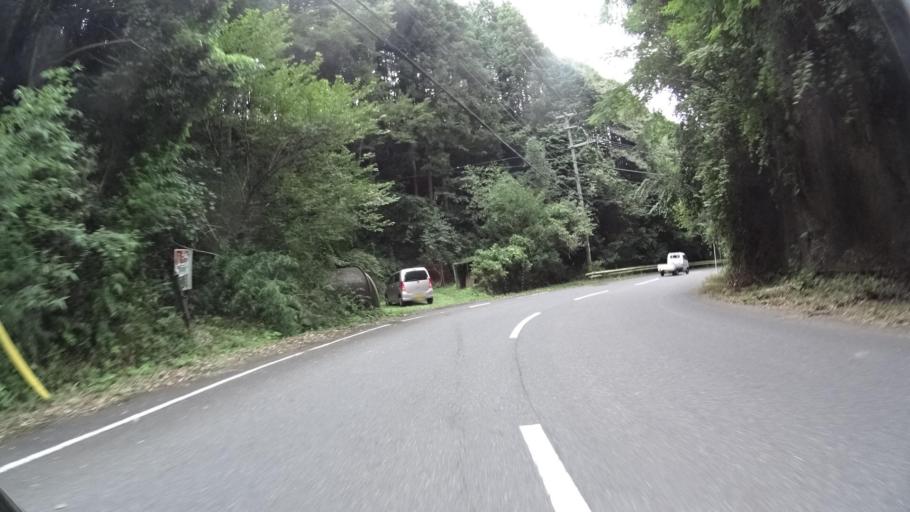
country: JP
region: Mie
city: Nabari
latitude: 34.7077
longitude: 136.0432
